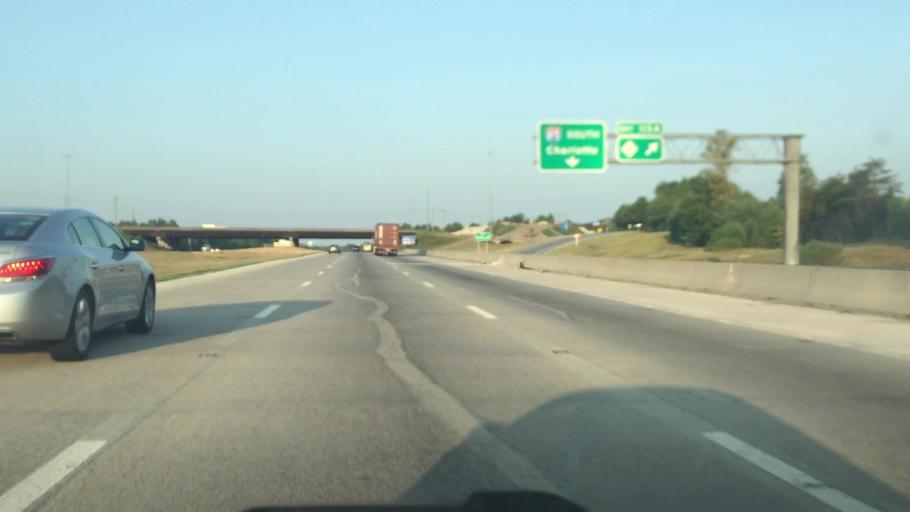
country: US
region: North Carolina
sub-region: Randolph County
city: Archdale
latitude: 35.9247
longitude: -79.9328
